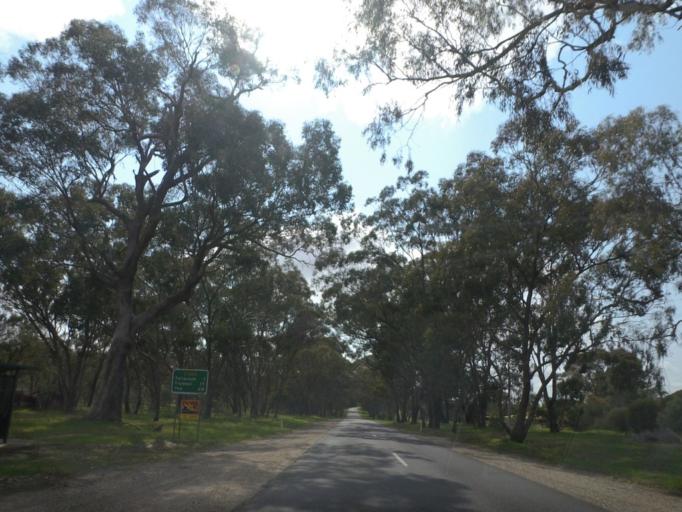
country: AU
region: Victoria
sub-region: Murrindindi
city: Kinglake West
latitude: -37.1052
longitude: 145.0955
